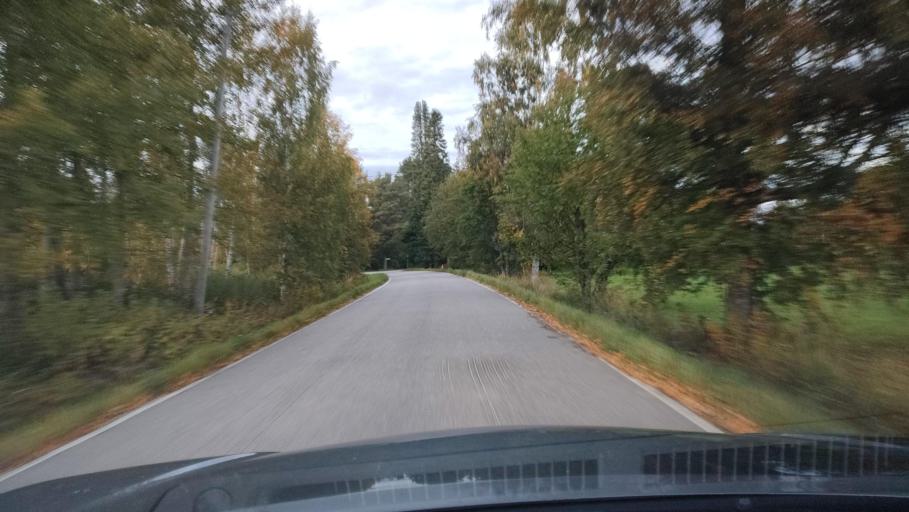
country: FI
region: Ostrobothnia
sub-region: Sydosterbotten
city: Kristinestad
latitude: 62.2563
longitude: 21.5098
